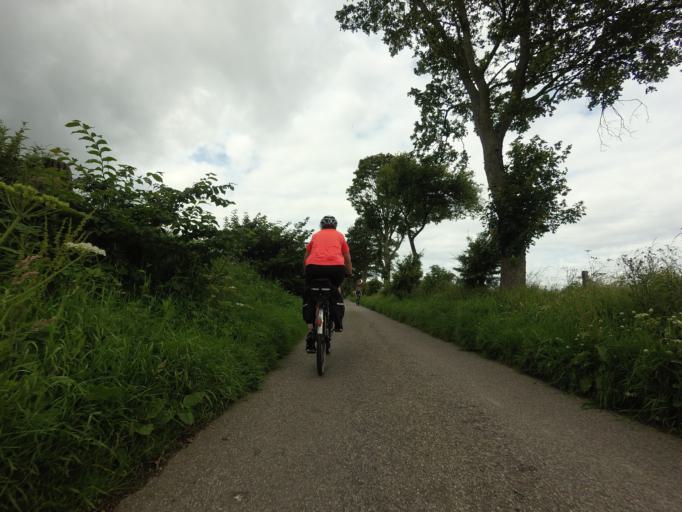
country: GB
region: Scotland
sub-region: Moray
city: Forres
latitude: 57.6131
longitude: -3.6469
